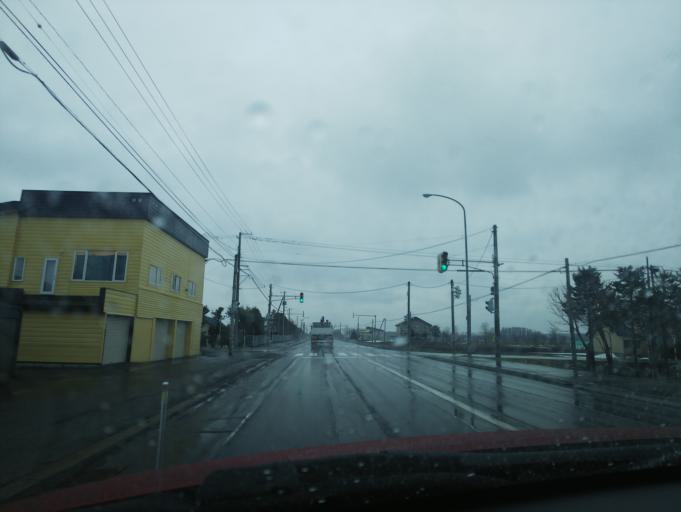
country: JP
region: Hokkaido
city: Nayoro
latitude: 44.2104
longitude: 142.3948
